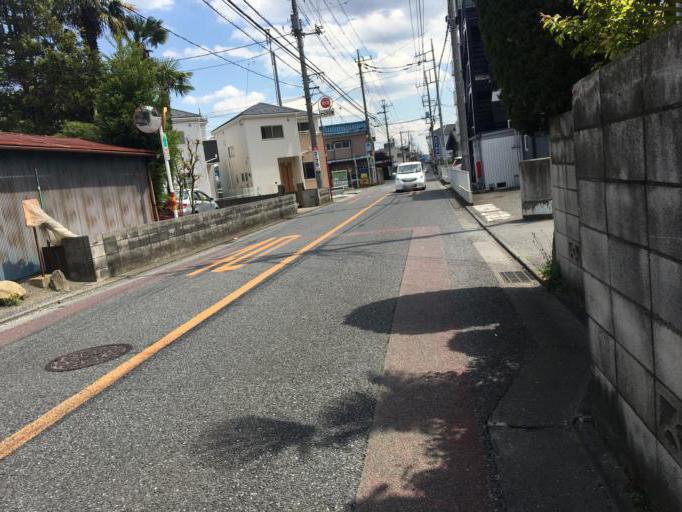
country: JP
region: Saitama
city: Kawagoe
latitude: 35.9313
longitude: 139.4742
